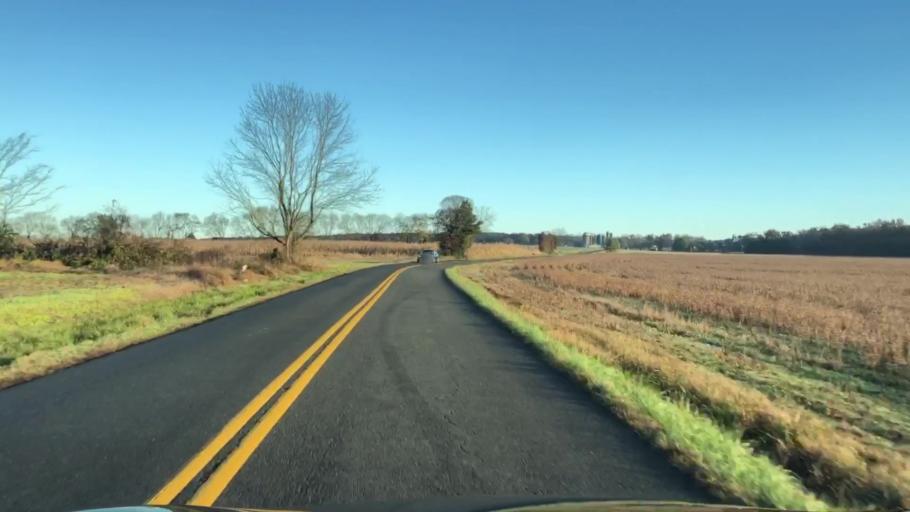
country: US
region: Virginia
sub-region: Prince William County
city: Nokesville
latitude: 38.6678
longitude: -77.6732
